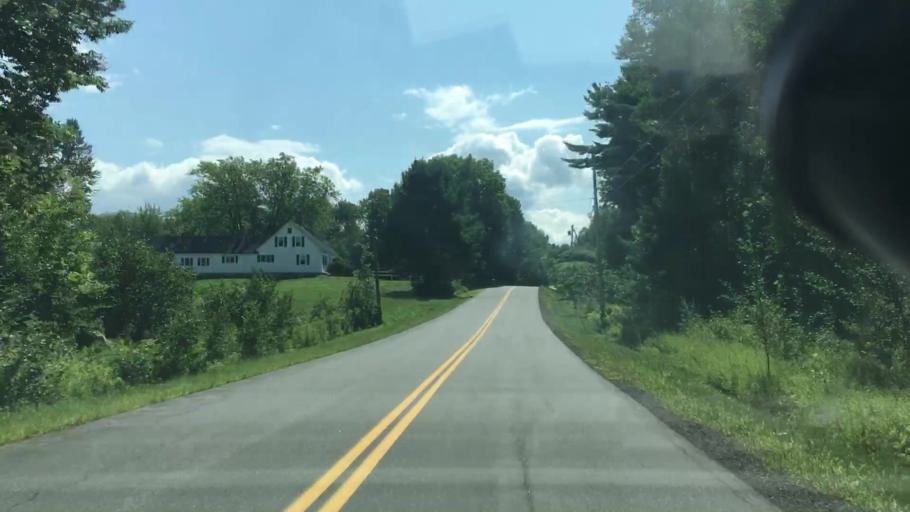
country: US
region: Maine
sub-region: Somerset County
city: Skowhegan
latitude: 44.6973
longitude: -69.6940
